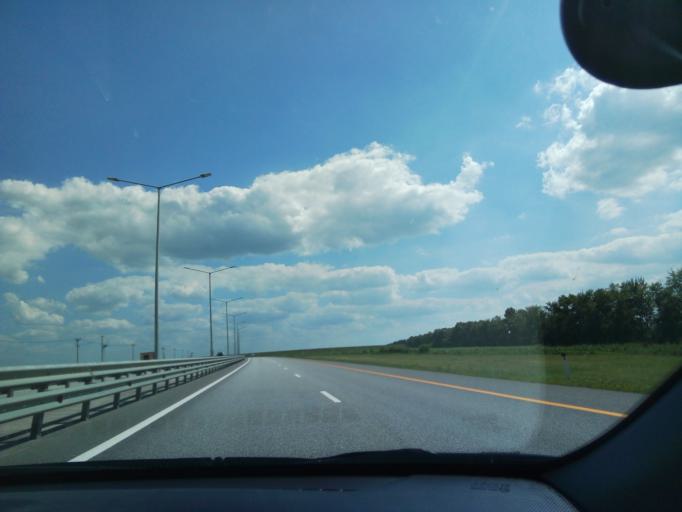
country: RU
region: Voronezj
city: Podkletnoye
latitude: 51.5146
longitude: 39.5119
